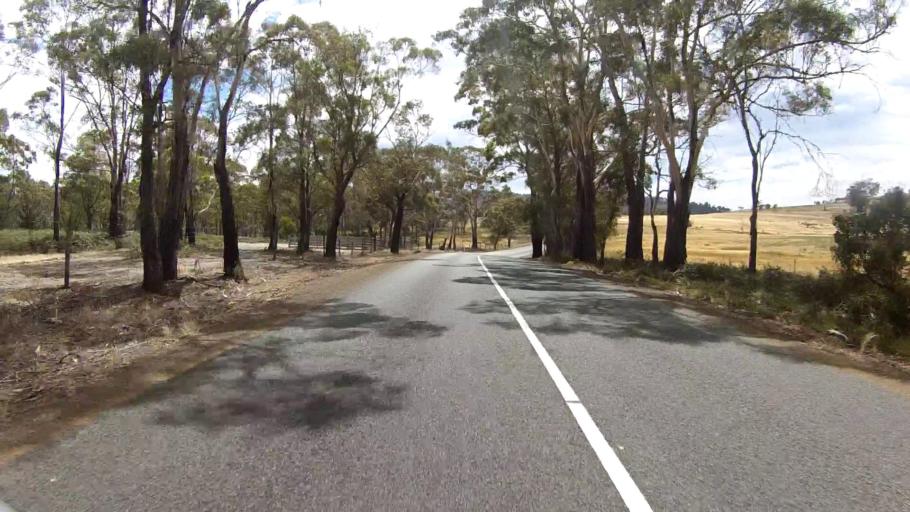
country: AU
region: Tasmania
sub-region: Sorell
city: Sorell
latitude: -42.8776
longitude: 147.6777
